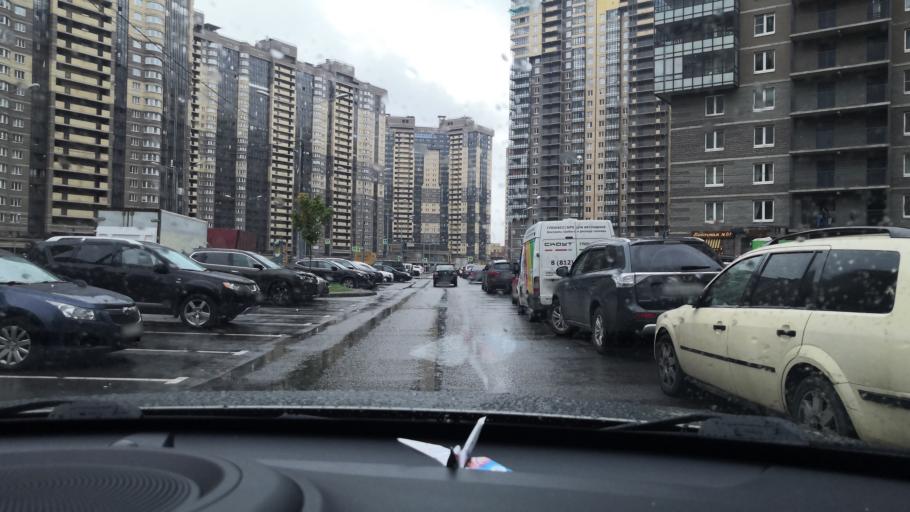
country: RU
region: Leningrad
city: Parnas
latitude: 60.0807
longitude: 30.3422
